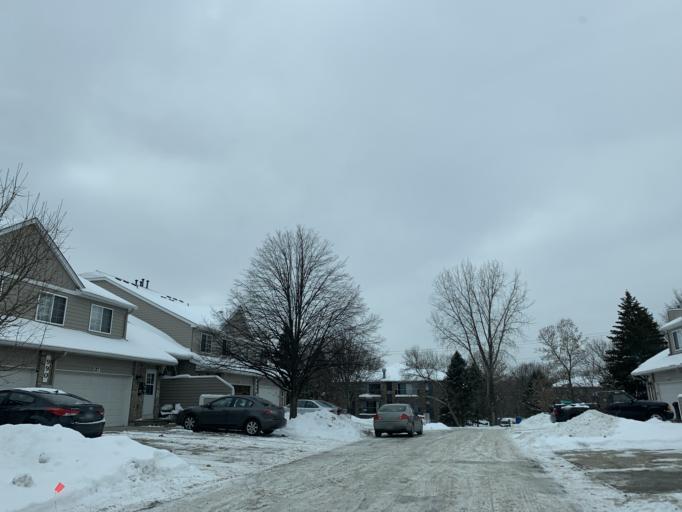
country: US
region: Minnesota
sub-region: Anoka County
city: Coon Rapids
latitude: 45.1632
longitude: -93.2912
